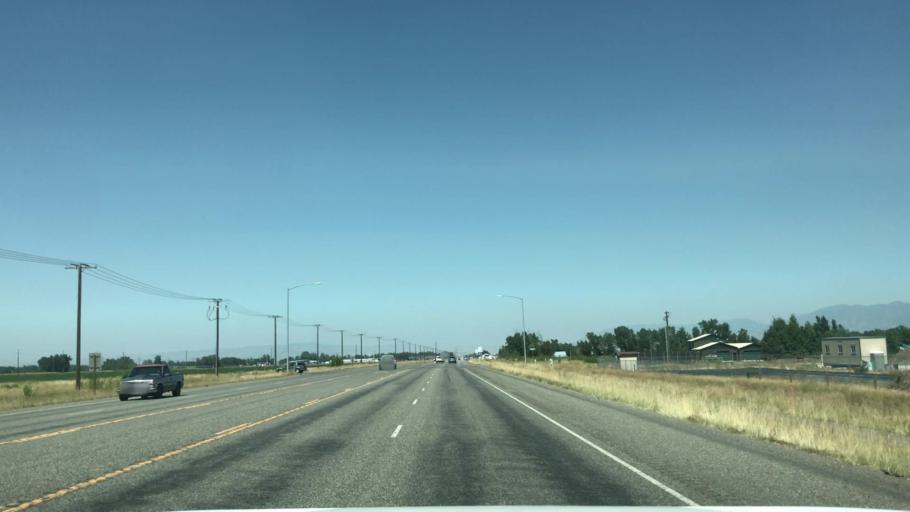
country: US
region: Montana
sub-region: Gallatin County
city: Four Corners
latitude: 45.6843
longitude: -111.1858
